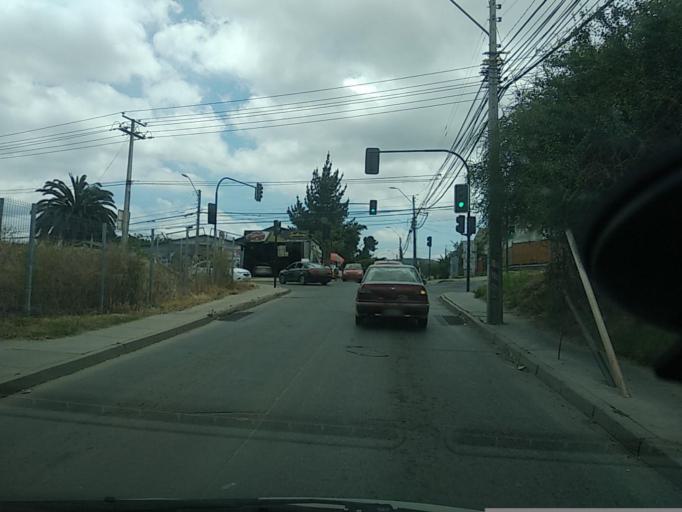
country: CL
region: Valparaiso
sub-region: Provincia de Marga Marga
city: Villa Alemana
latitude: -33.0434
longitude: -71.4052
